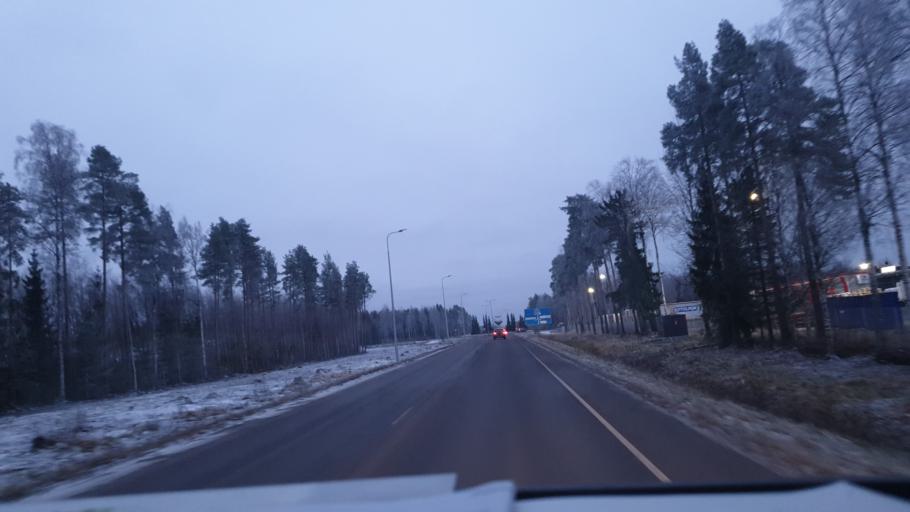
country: FI
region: Southern Ostrobothnia
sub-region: Seinaejoki
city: Nurmo
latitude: 62.7890
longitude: 22.8987
